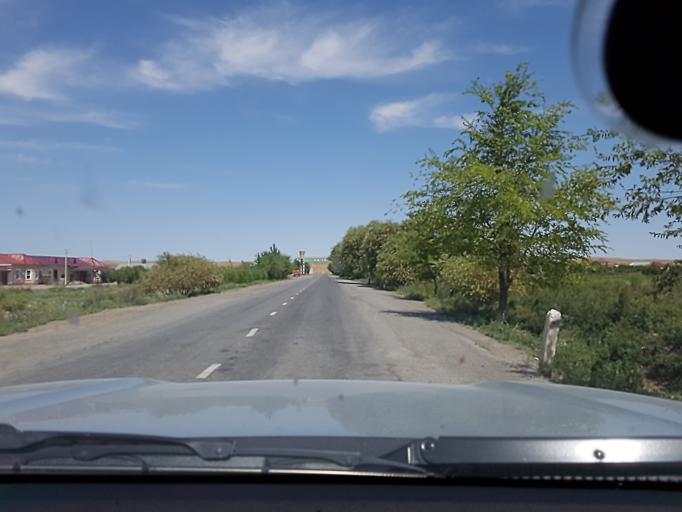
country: UZ
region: Karakalpakstan
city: Mang'it Shahri
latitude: 42.2414
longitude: 60.1474
